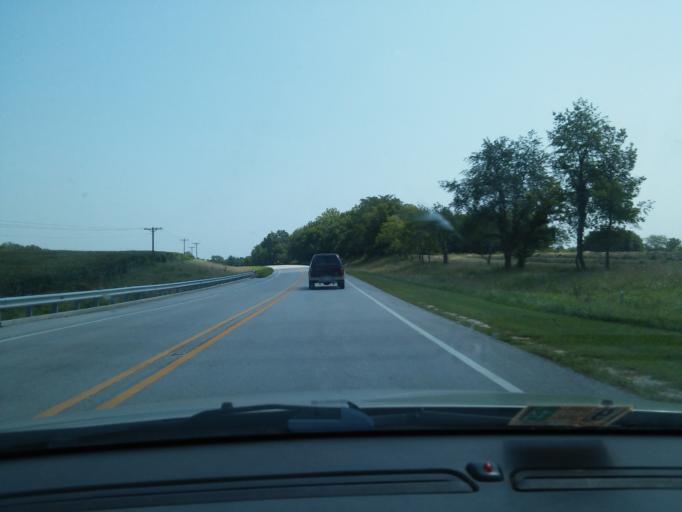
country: US
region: Missouri
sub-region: Pike County
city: Louisiana
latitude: 39.5263
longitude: -90.9339
